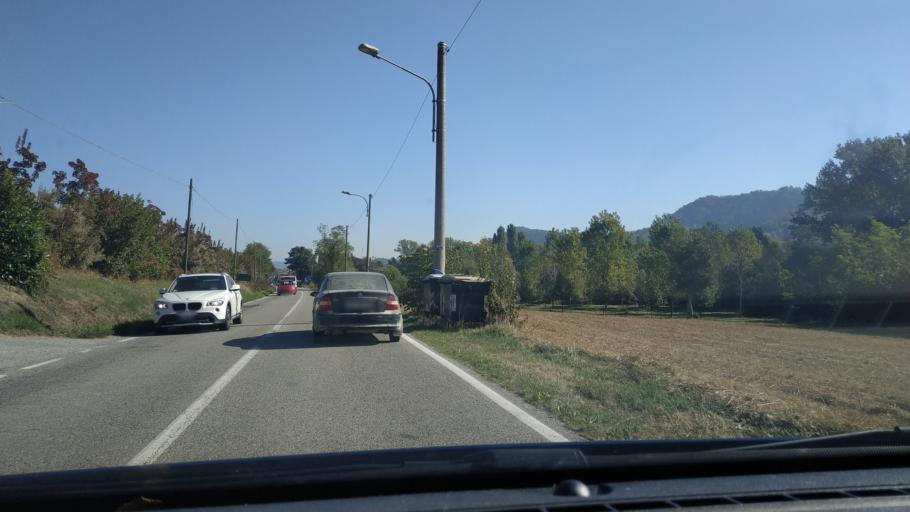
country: IT
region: Piedmont
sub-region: Provincia di Alessandria
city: Villadeati
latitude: 45.0853
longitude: 8.1733
